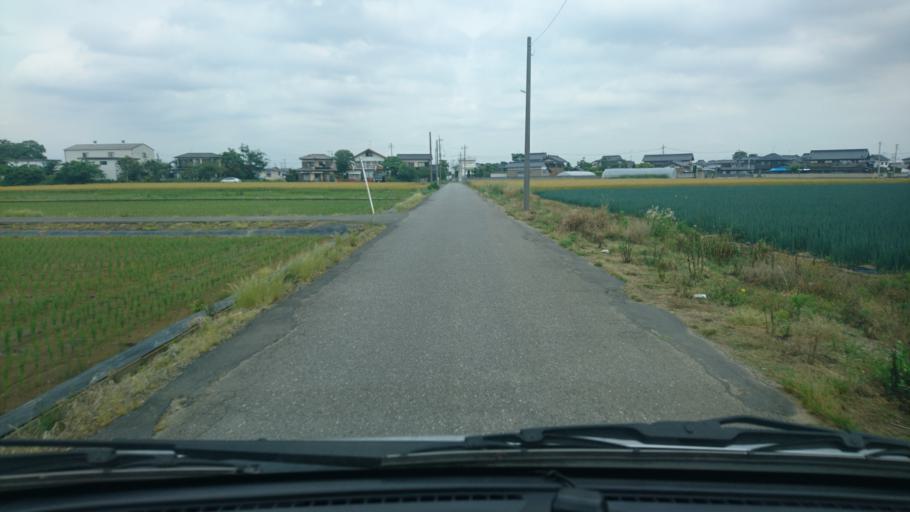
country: JP
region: Ibaraki
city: Ishige
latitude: 36.1003
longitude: 139.9783
